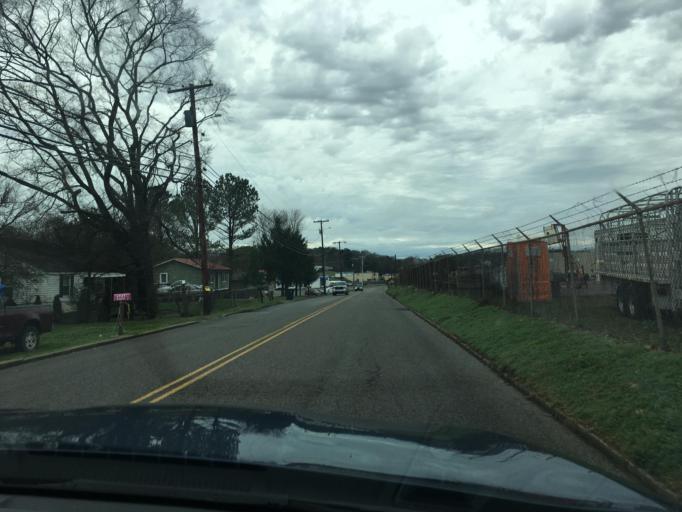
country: US
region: Tennessee
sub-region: McMinn County
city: Athens
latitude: 35.4623
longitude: -84.6066
